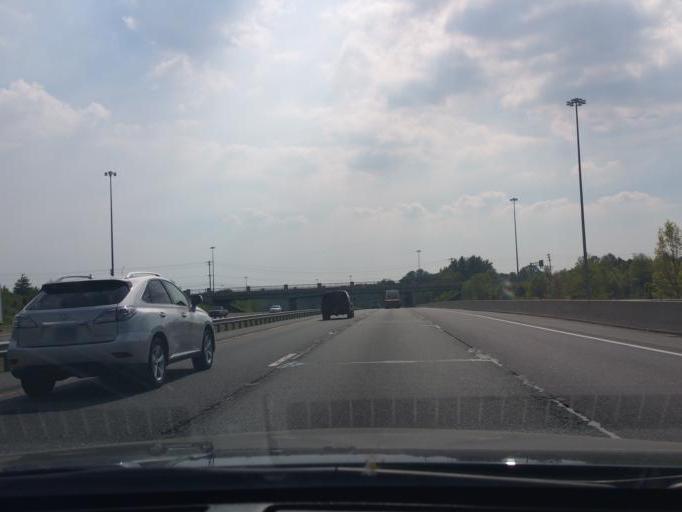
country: US
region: Maryland
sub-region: Harford County
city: Aberdeen
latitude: 39.5278
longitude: -76.1891
